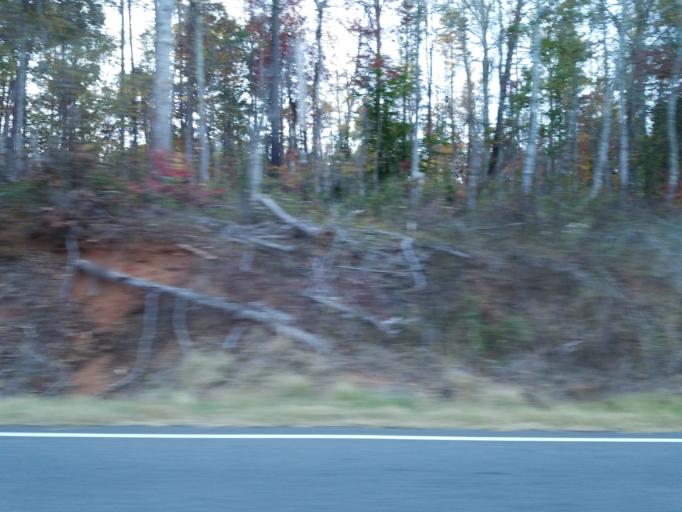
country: US
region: Georgia
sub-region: Lumpkin County
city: Dahlonega
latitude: 34.5292
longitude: -84.0162
